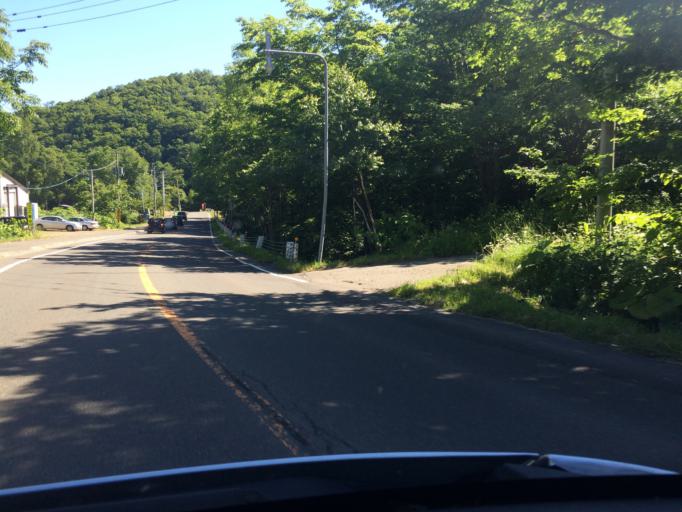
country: JP
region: Hokkaido
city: Sapporo
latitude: 43.0239
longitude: 141.2883
